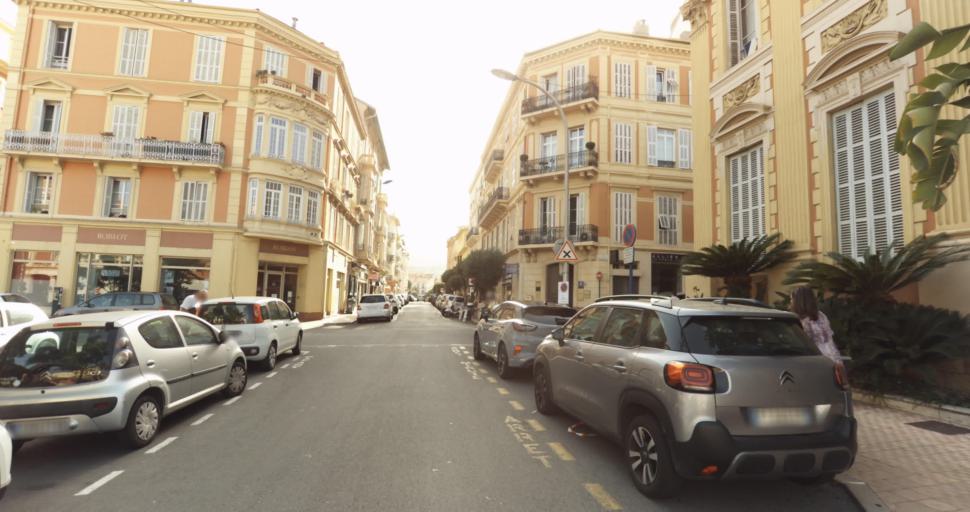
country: FR
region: Provence-Alpes-Cote d'Azur
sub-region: Departement des Alpes-Maritimes
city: Menton
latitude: 43.7755
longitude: 7.5028
